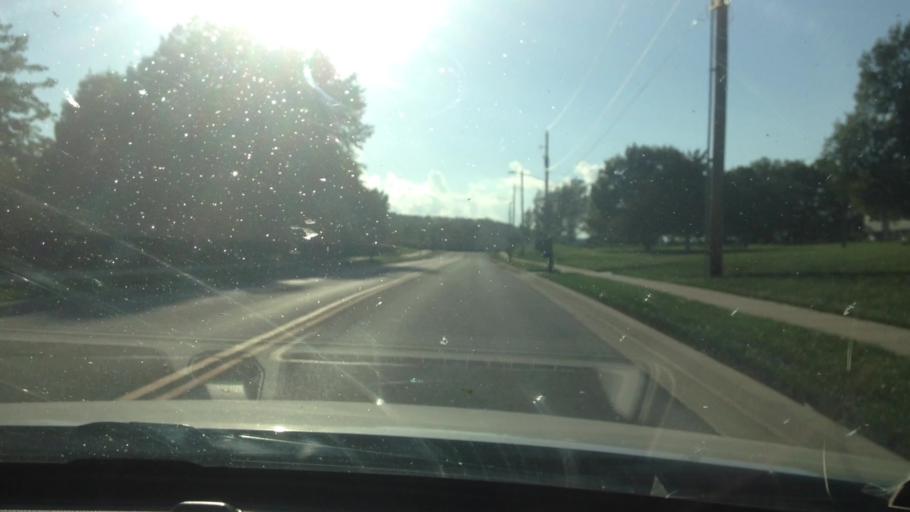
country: US
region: Kansas
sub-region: Leavenworth County
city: Leavenworth
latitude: 39.2885
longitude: -94.9443
